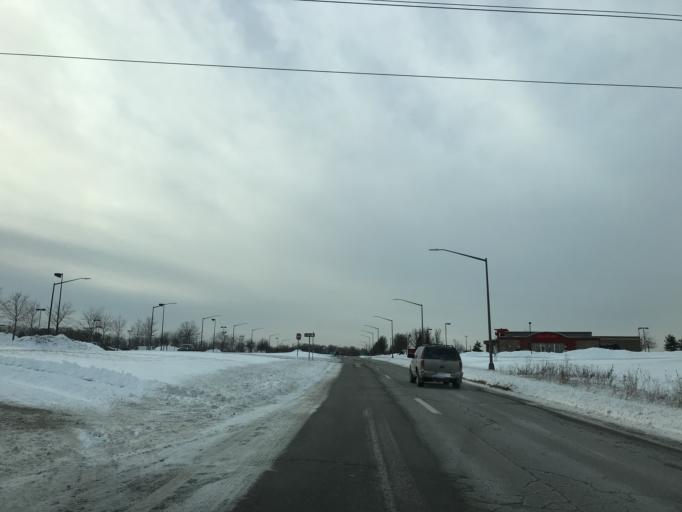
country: US
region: Michigan
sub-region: Oakland County
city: Wolverine Lake
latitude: 42.5352
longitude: -83.4423
